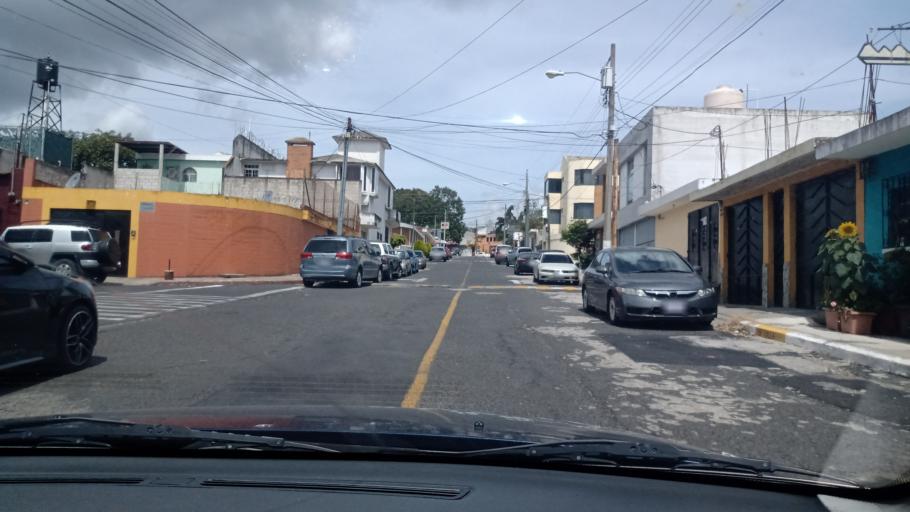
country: GT
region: Guatemala
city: Guatemala City
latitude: 14.6481
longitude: -90.4632
